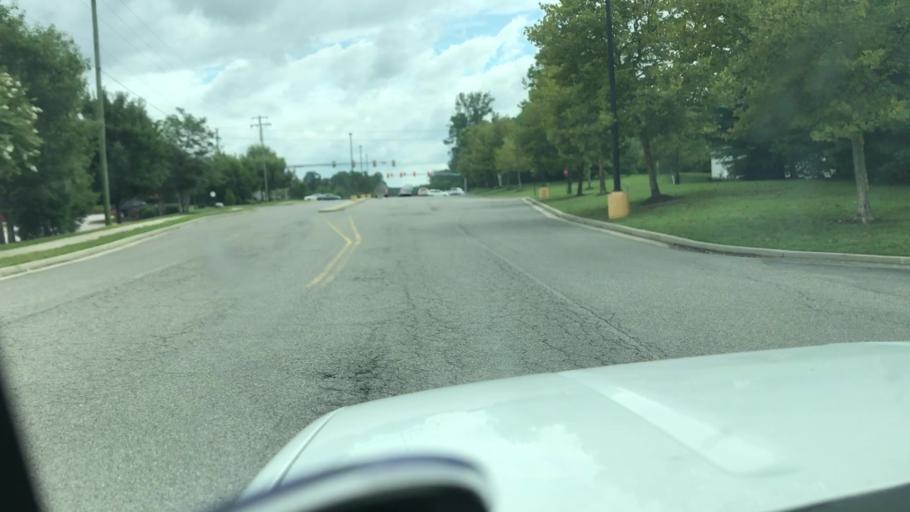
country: US
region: Virginia
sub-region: Henrico County
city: Short Pump
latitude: 37.6521
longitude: -77.6068
